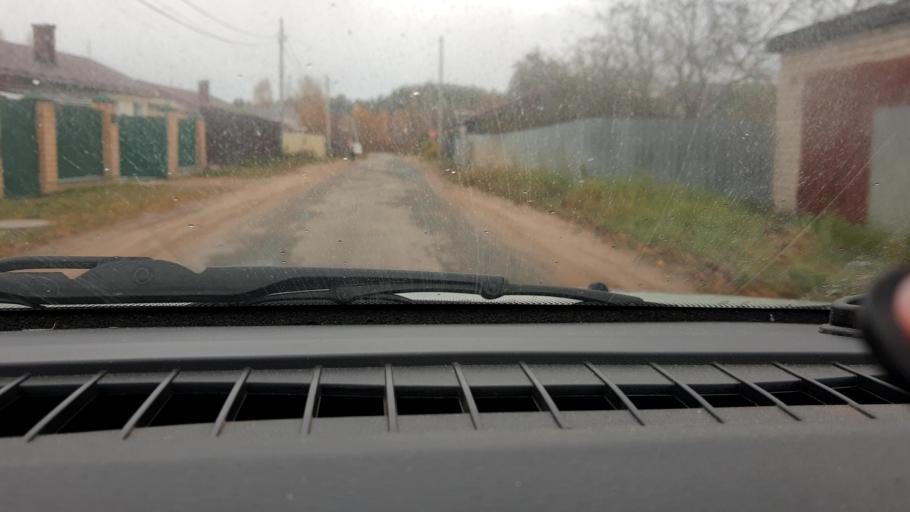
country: RU
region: Nizjnij Novgorod
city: Sitniki
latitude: 56.4138
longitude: 44.0379
